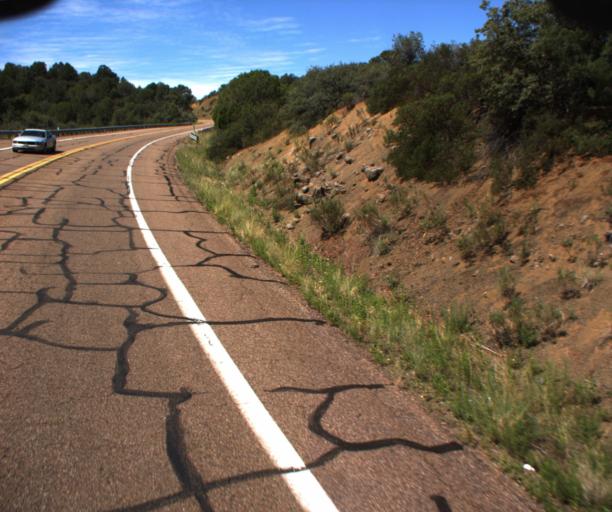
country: US
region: Arizona
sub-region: Navajo County
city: Cibecue
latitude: 33.7742
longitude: -110.5062
